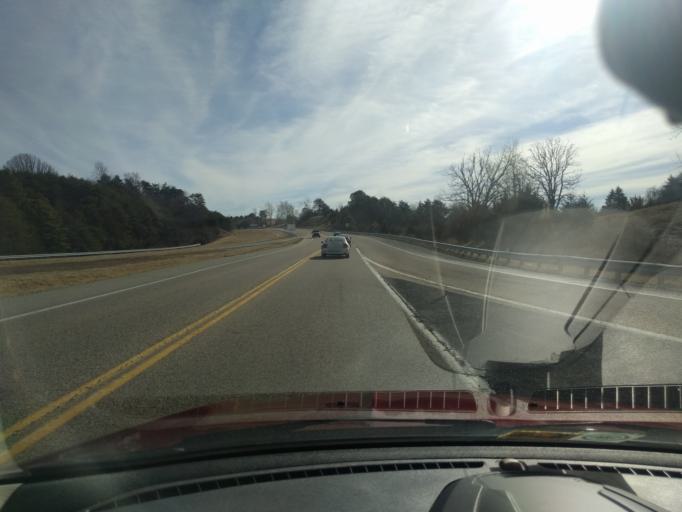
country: US
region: Virginia
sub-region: Augusta County
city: Jolivue
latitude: 38.1301
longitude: -79.0916
